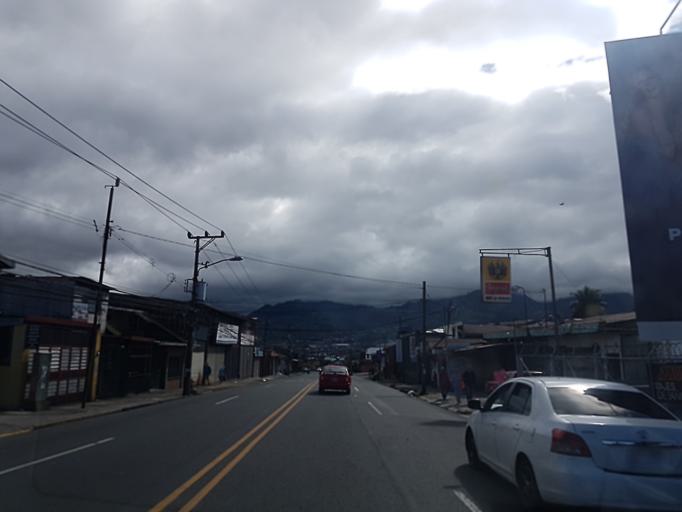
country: CR
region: San Jose
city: San Jose
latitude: 9.9251
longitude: -84.0916
